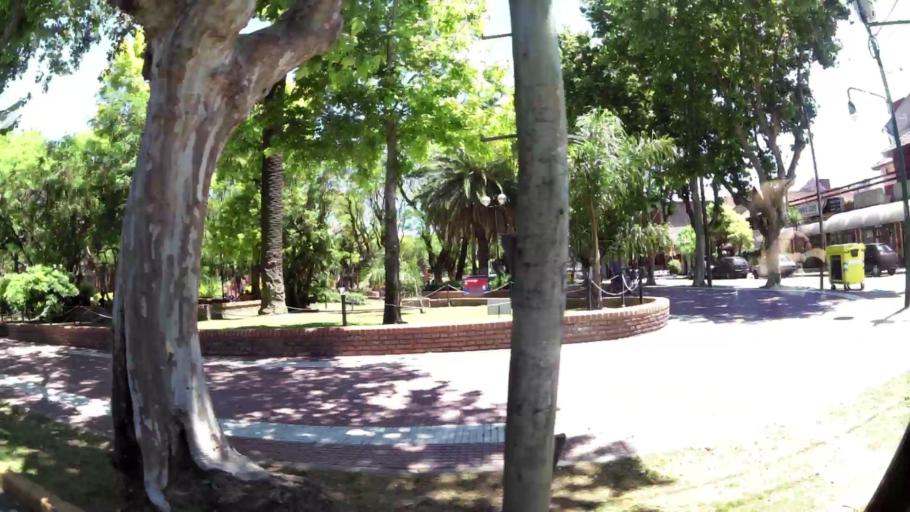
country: AR
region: Buenos Aires
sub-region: Partido de San Isidro
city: San Isidro
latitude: -34.4915
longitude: -58.5100
